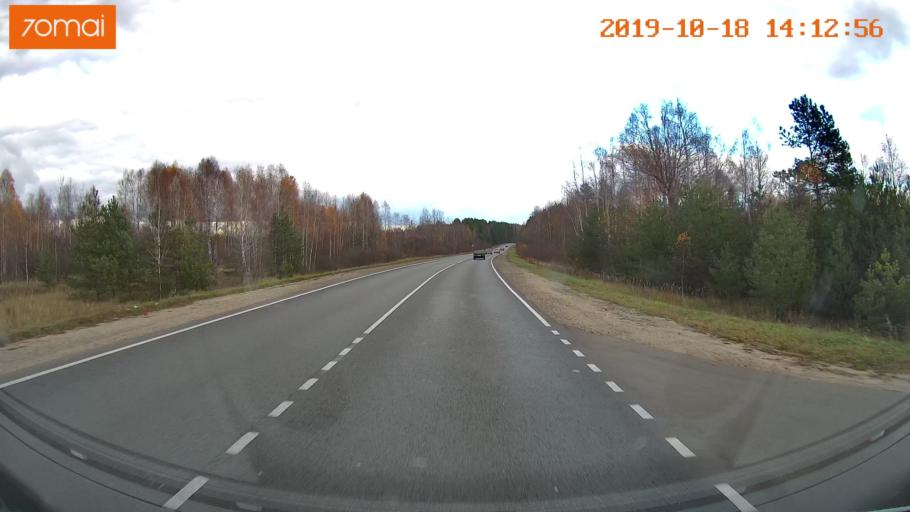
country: RU
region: Rjazan
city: Spas-Klepiki
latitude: 55.1497
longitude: 40.2605
